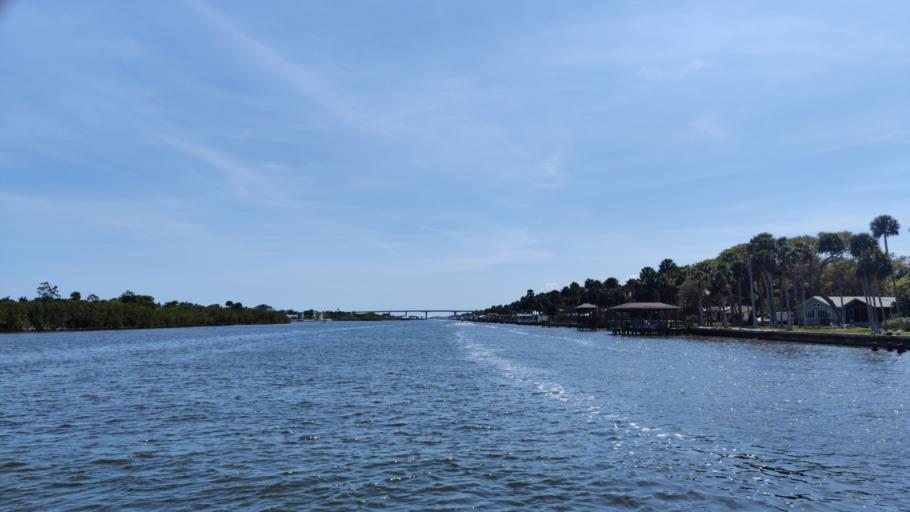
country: US
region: Florida
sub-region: Flagler County
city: Flagler Beach
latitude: 29.4919
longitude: -81.1413
